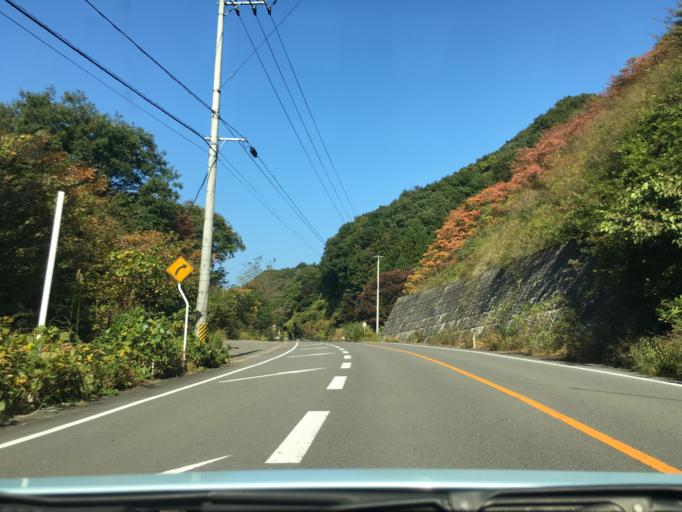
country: JP
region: Fukushima
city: Sukagawa
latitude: 37.2975
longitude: 140.1596
